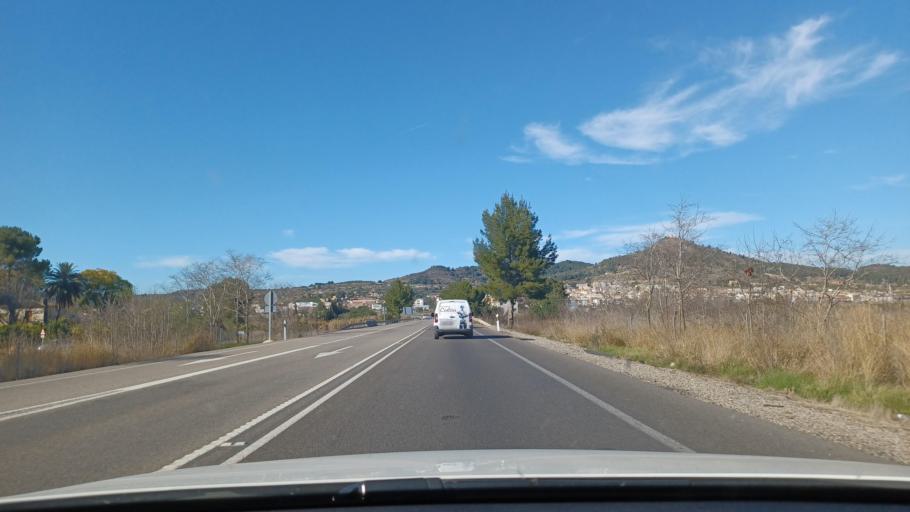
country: ES
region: Valencia
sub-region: Provincia de Valencia
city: Llosa de Ranes
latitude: 39.0080
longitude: -0.5319
